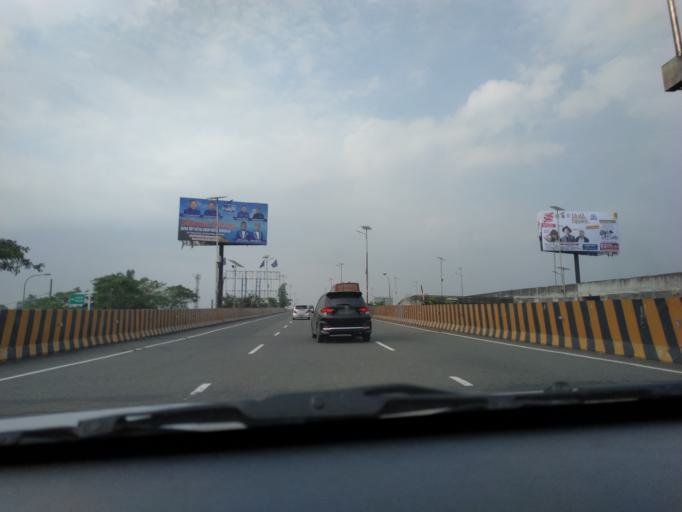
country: ID
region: North Sumatra
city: Percut
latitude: 3.6109
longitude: 98.8549
